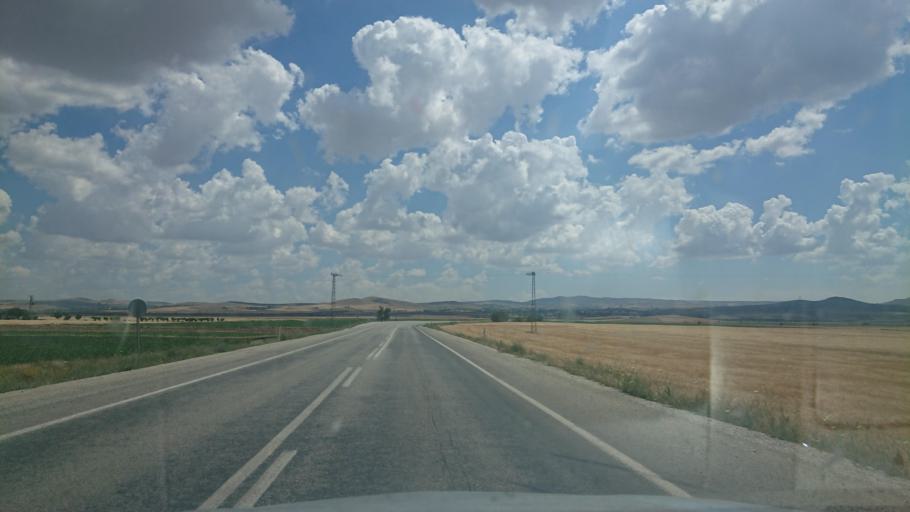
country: TR
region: Aksaray
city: Sariyahsi
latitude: 39.0155
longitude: 33.8674
